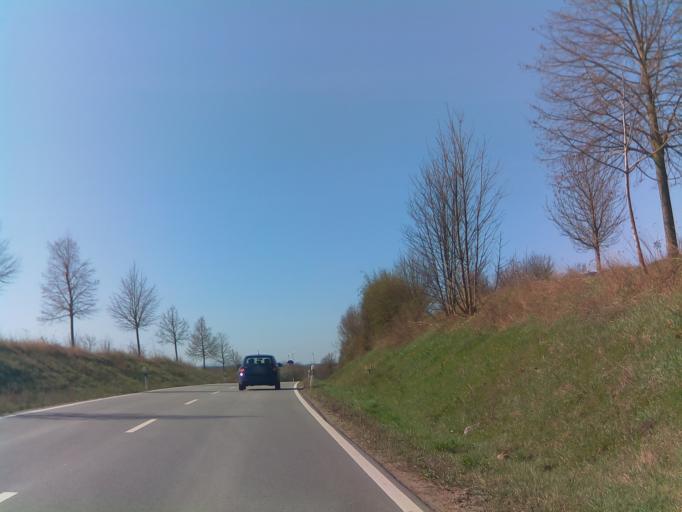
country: DE
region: Rheinland-Pfalz
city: Mommenheim
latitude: 49.8827
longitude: 8.2616
